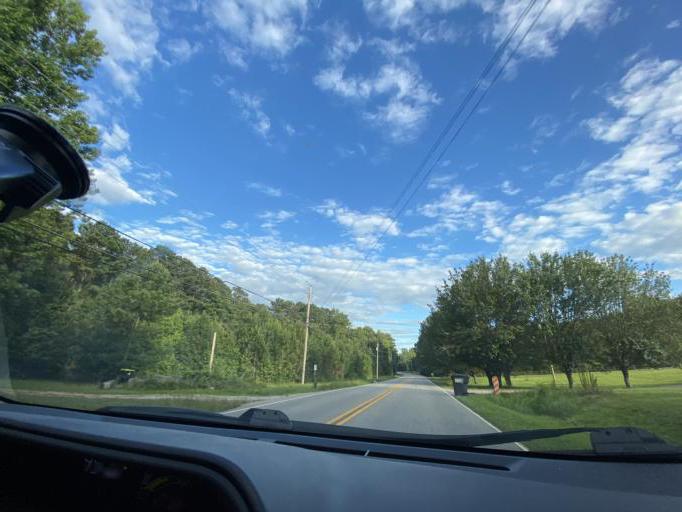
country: US
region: Georgia
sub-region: Fayette County
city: Tyrone
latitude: 33.4395
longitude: -84.6539
